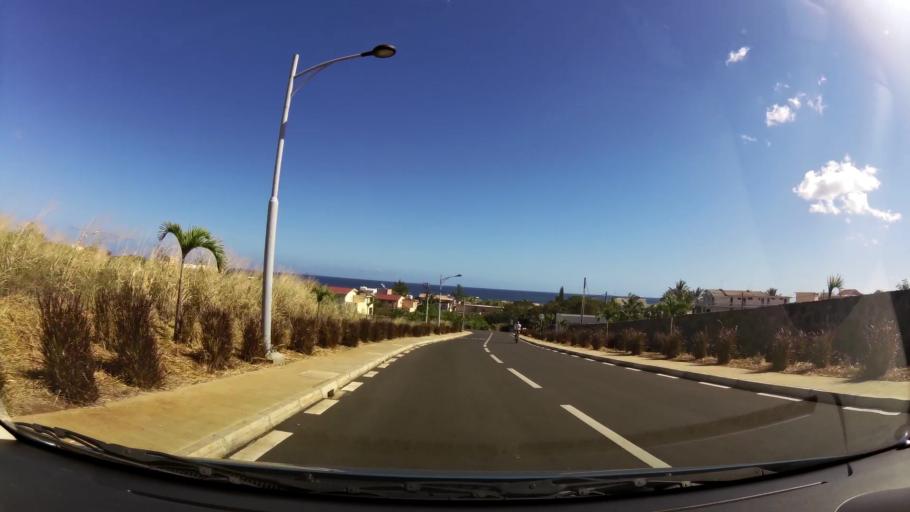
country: MU
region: Black River
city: Flic en Flac
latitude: -20.2659
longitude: 57.3792
